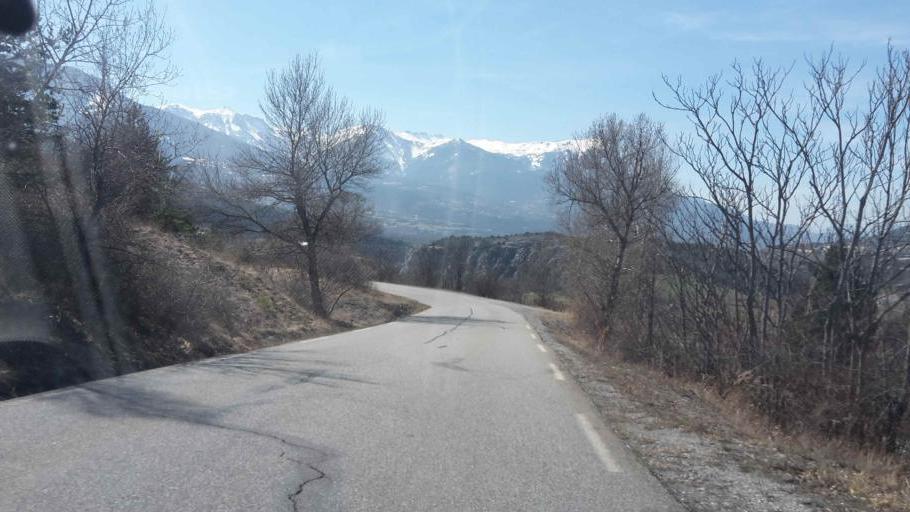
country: FR
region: Provence-Alpes-Cote d'Azur
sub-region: Departement des Hautes-Alpes
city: Embrun
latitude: 44.5728
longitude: 6.5238
